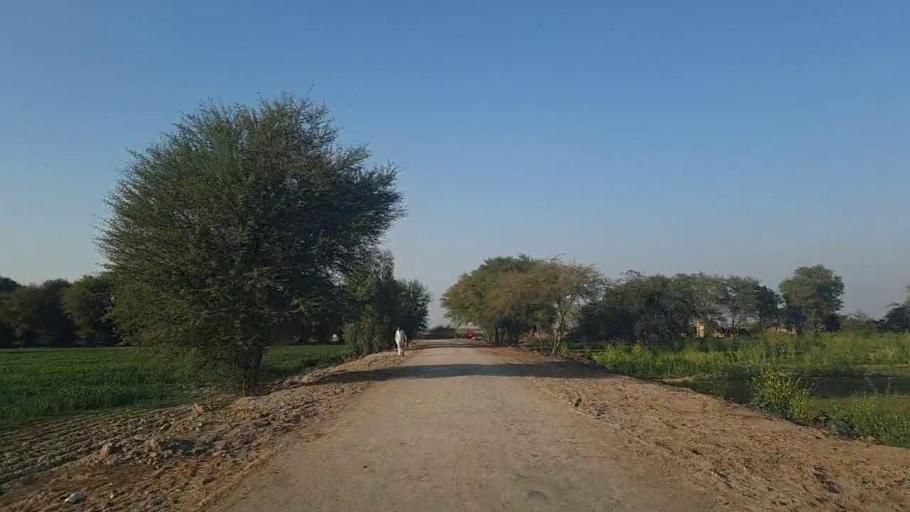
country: PK
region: Sindh
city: Jam Sahib
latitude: 26.3068
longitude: 68.6703
